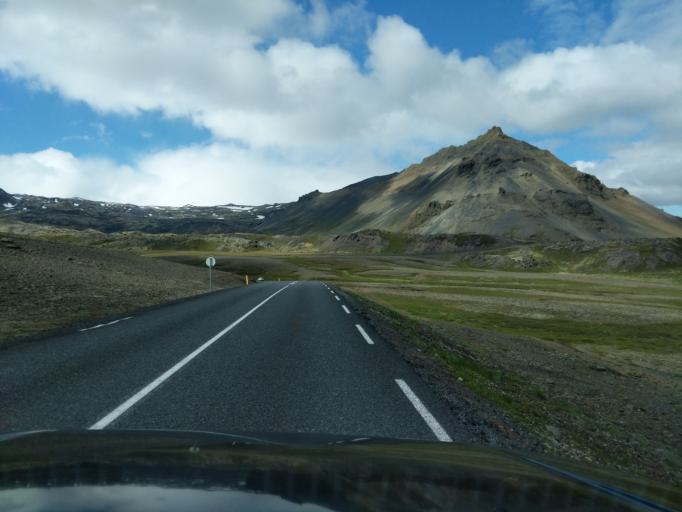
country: IS
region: West
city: Olafsvik
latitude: 64.7568
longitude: -23.6707
